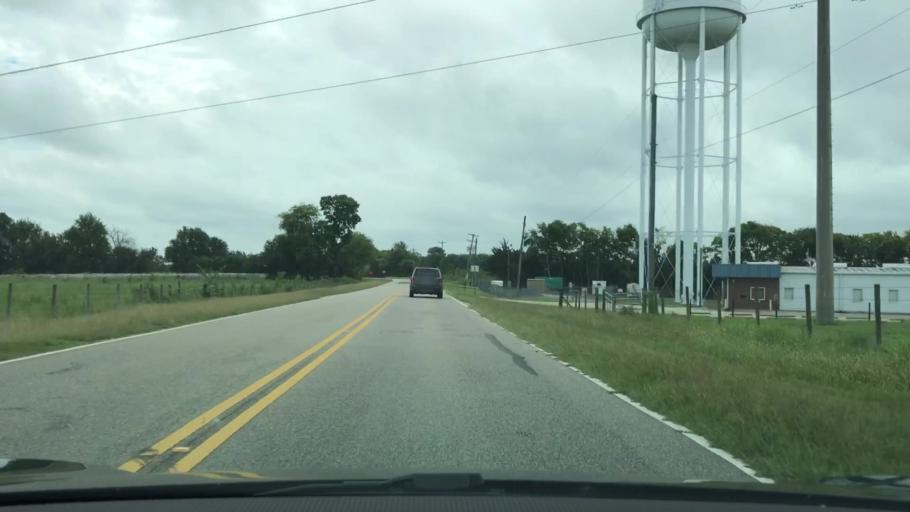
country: US
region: Alabama
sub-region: Montgomery County
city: Pike Road
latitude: 32.2839
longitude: -86.0872
